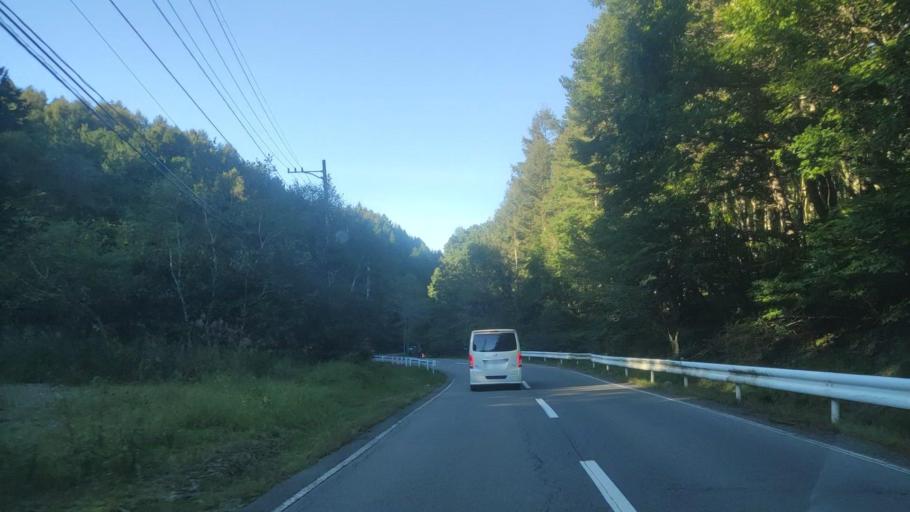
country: JP
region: Nagano
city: Kamimaruko
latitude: 36.2182
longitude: 138.2933
